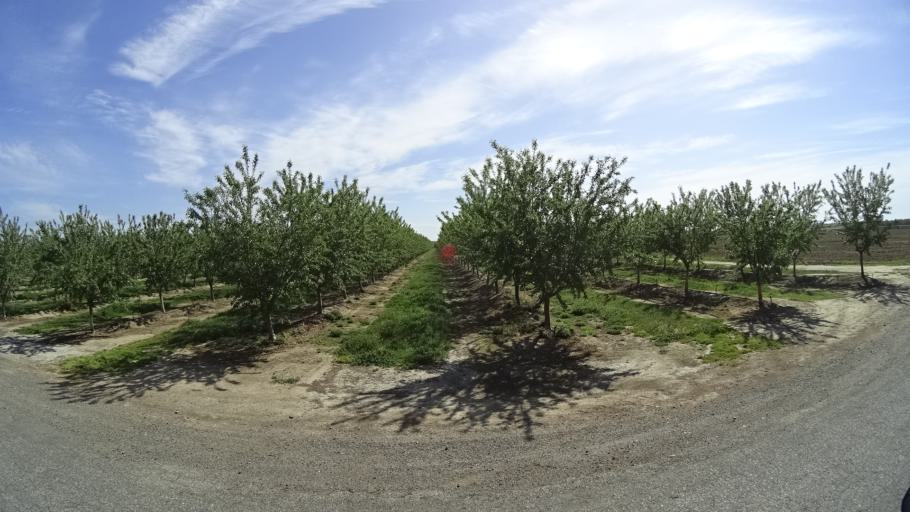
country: US
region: California
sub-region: Glenn County
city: Hamilton City
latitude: 39.6417
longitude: -122.0181
